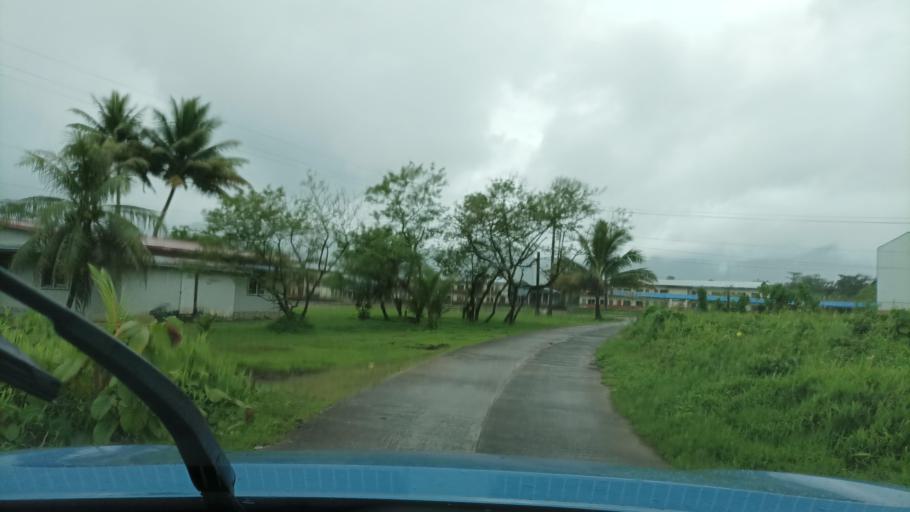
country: FM
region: Pohnpei
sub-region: Kolonia Municipality
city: Kolonia
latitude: 6.9550
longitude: 158.2213
